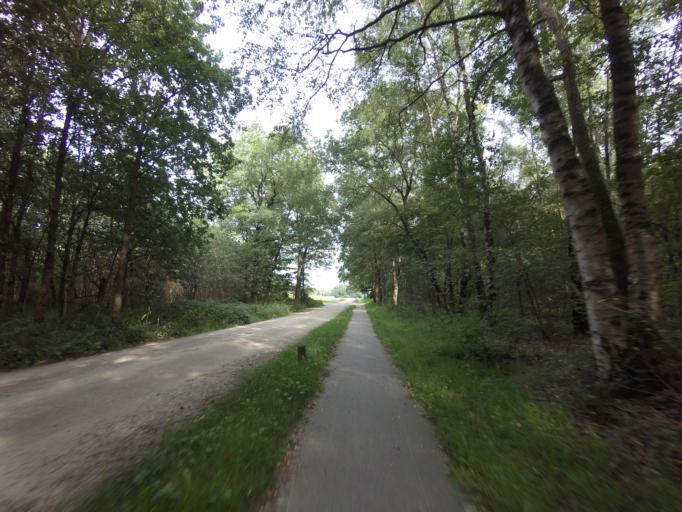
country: DE
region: Lower Saxony
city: Getelo
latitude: 52.4516
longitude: 6.8296
